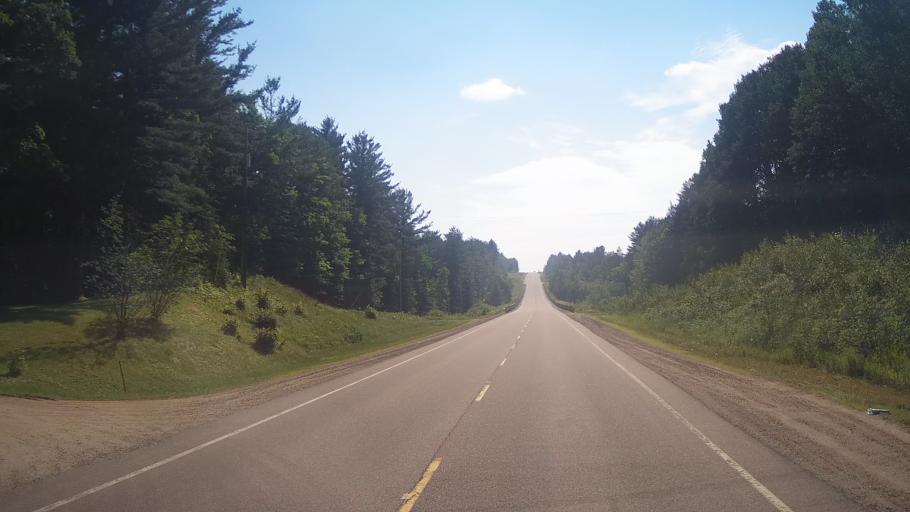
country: CA
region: Ontario
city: Petawawa
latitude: 45.5301
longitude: -77.4949
